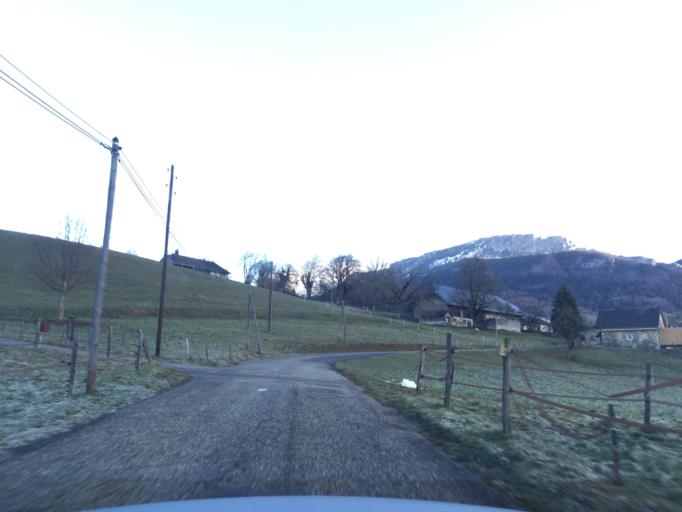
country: FR
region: Rhone-Alpes
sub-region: Departement de la Haute-Savoie
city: Gruffy
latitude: 45.7344
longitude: 6.1212
